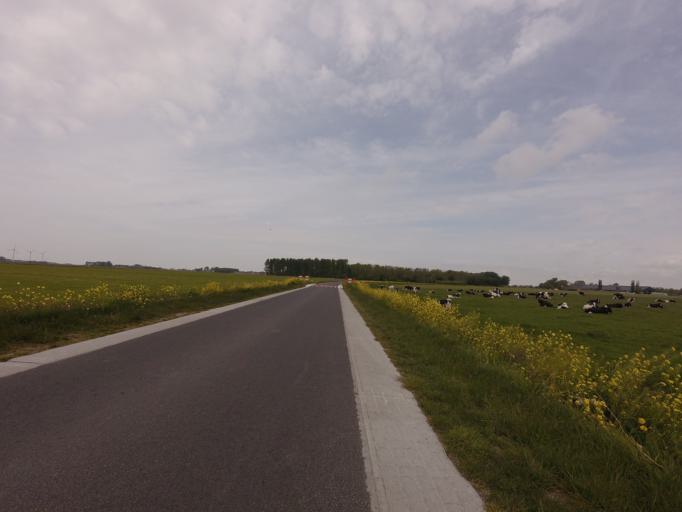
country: NL
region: Friesland
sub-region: Sudwest Fryslan
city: Bolsward
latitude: 53.0913
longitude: 5.4790
